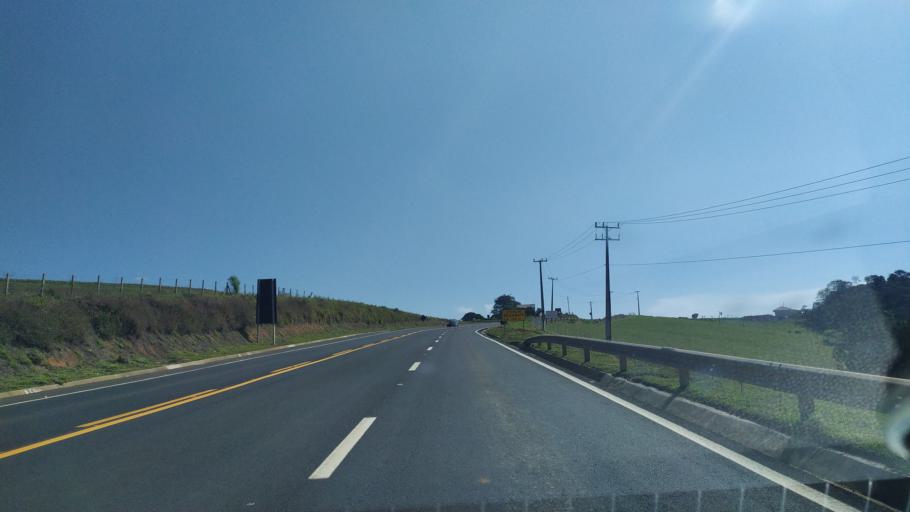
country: BR
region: Parana
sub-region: Telemaco Borba
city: Telemaco Borba
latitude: -24.2845
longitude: -50.7111
